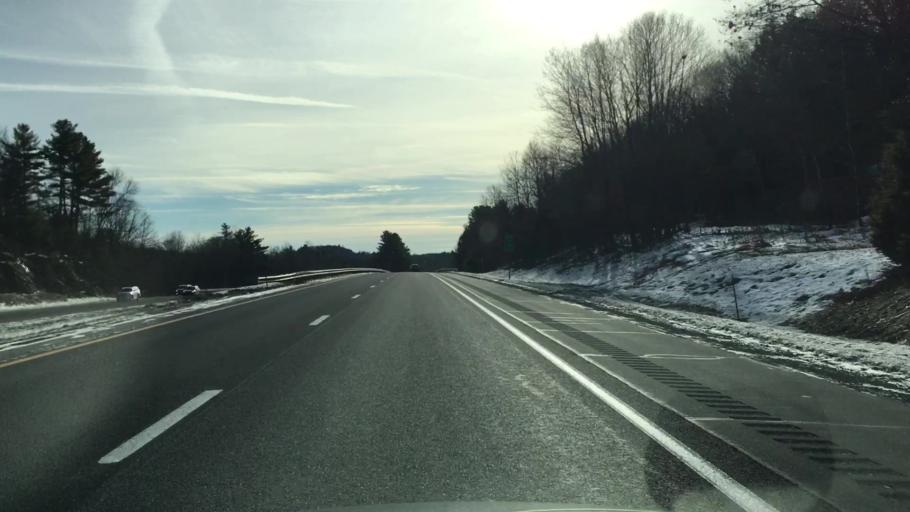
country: US
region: New Hampshire
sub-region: Sullivan County
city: Grantham
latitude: 43.5353
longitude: -72.1394
